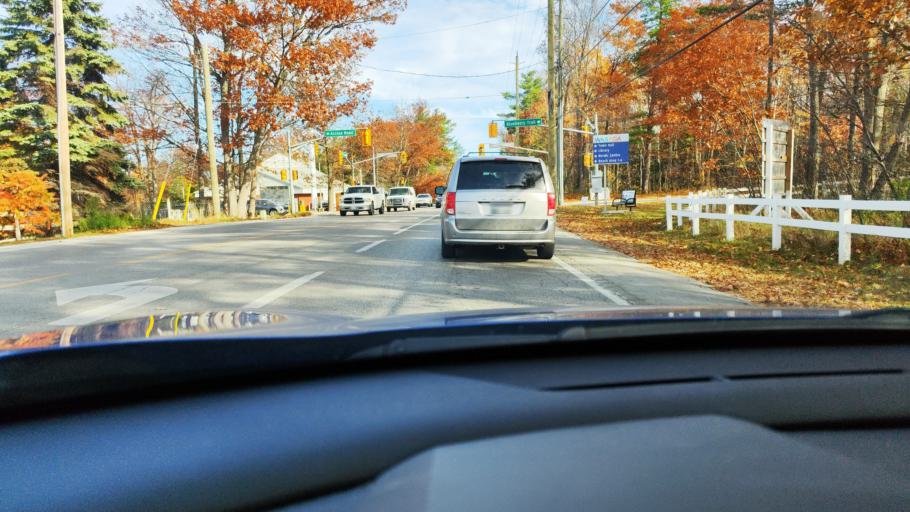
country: CA
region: Ontario
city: Wasaga Beach
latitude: 44.5182
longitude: -80.0186
